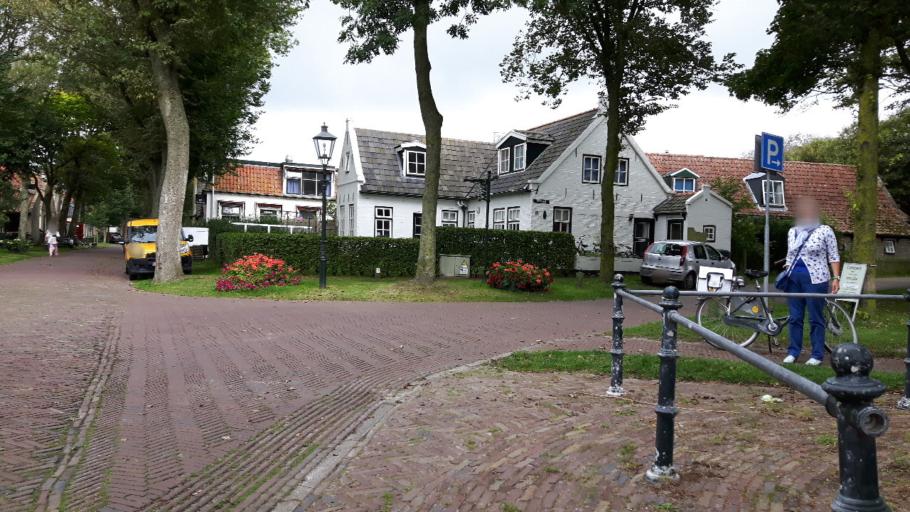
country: NL
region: Friesland
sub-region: Gemeente Ameland
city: Hollum
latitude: 53.4358
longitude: 5.6405
